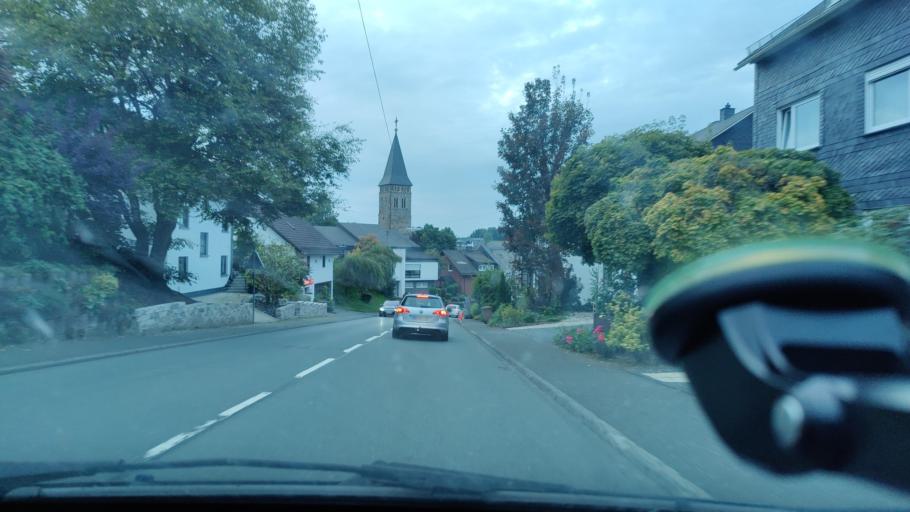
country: DE
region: North Rhine-Westphalia
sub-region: Regierungsbezirk Arnsberg
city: Wilnsdorf
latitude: 50.8134
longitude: 8.1046
